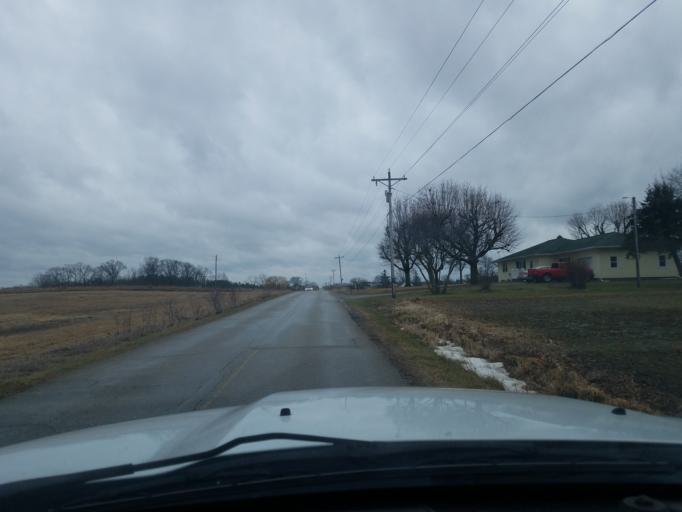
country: US
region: Indiana
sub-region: Noble County
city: Albion
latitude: 41.4172
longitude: -85.3955
